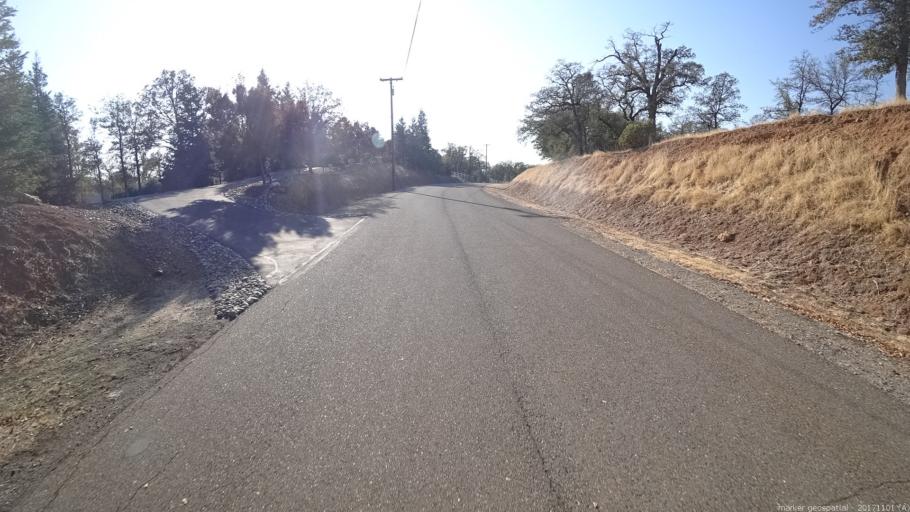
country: US
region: California
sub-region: Shasta County
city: Bella Vista
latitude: 40.6715
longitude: -122.2943
